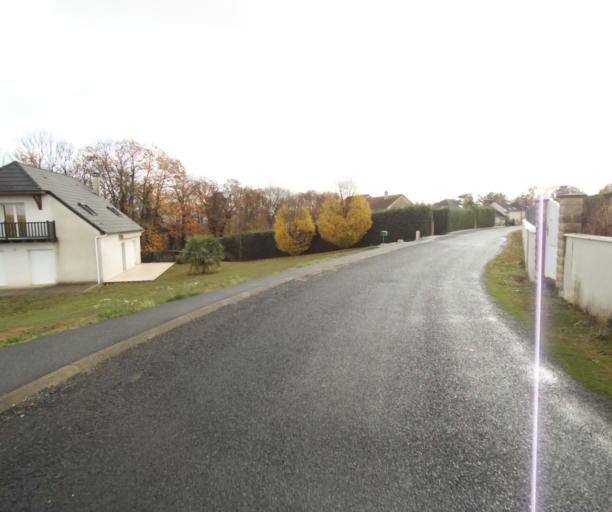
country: FR
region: Limousin
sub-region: Departement de la Correze
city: Cornil
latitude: 45.2206
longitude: 1.6447
